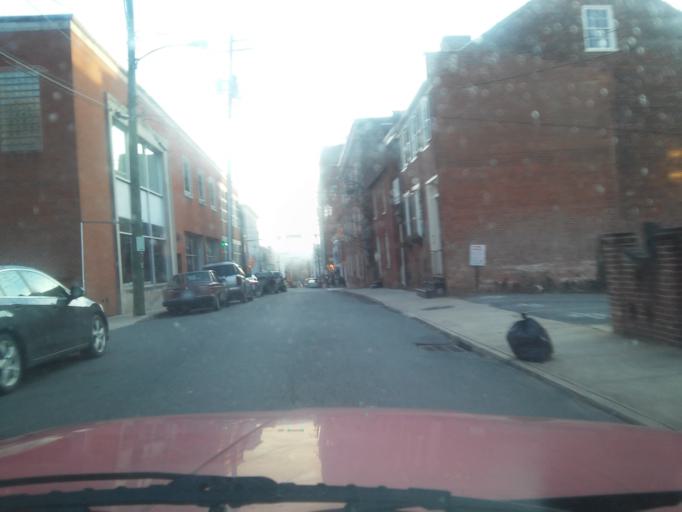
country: US
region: Virginia
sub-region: City of Charlottesville
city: Charlottesville
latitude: 38.0315
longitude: -78.4786
